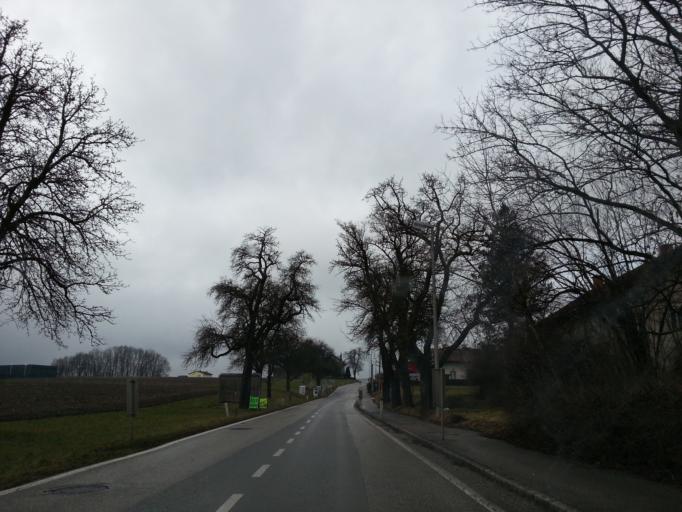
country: AT
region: Upper Austria
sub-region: Politischer Bezirk Ried im Innkreis
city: Ried im Innkreis
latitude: 48.2060
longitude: 13.4759
